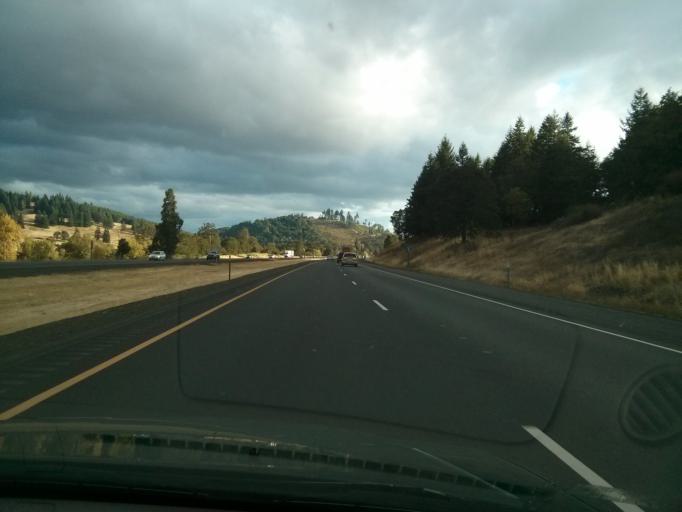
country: US
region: Oregon
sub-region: Douglas County
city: Yoncalla
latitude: 43.5119
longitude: -123.3159
